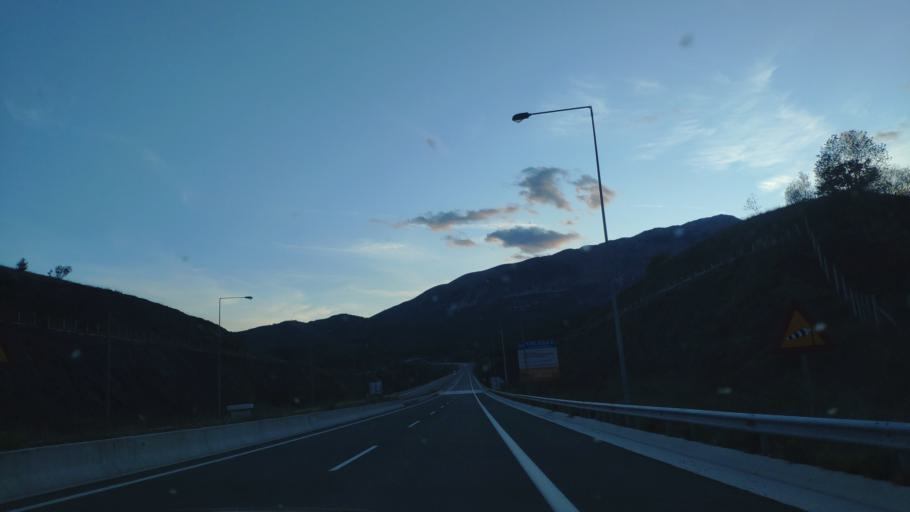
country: GR
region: Epirus
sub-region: Nomos Ioanninon
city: Katsikas
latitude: 39.7160
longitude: 20.9898
